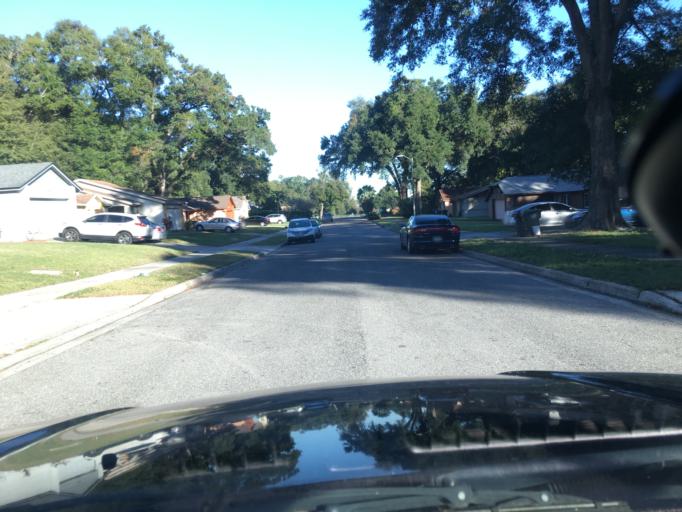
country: US
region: Florida
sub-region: Orange County
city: Lockhart
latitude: 28.6021
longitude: -81.4667
